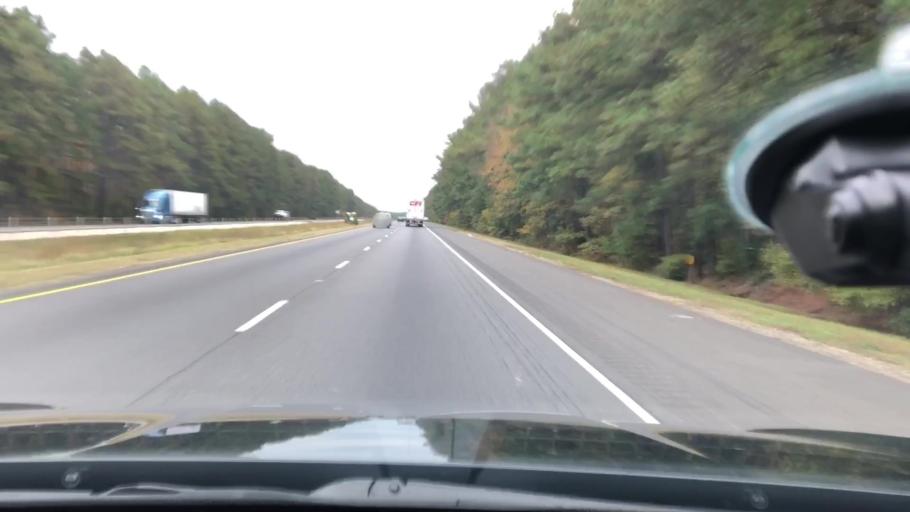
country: US
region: Arkansas
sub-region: Clark County
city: Arkadelphia
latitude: 34.2743
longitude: -92.9673
